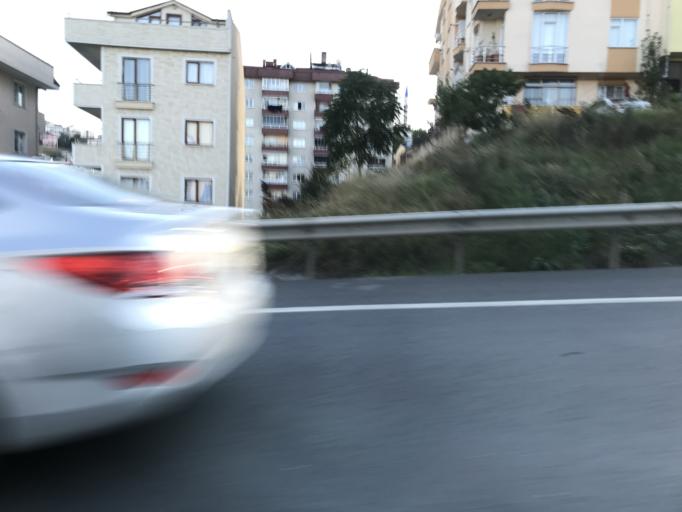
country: TR
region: Kocaeli
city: Darica
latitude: 40.7793
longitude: 29.4171
